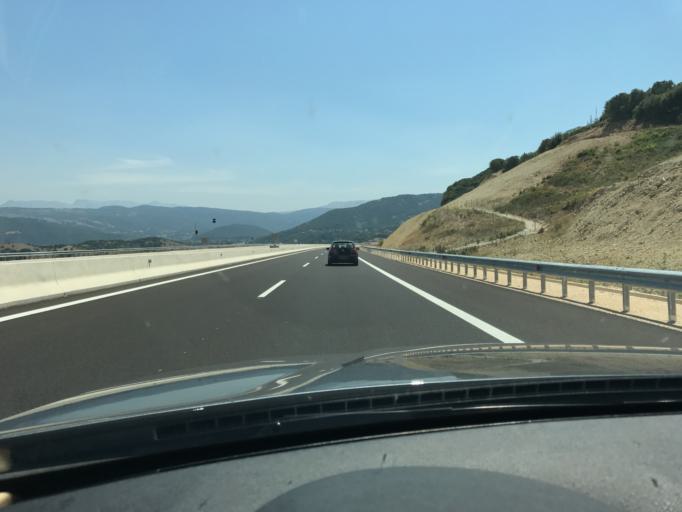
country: GR
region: Epirus
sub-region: Nomos Ioanninon
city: Pedini
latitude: 39.5596
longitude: 20.8313
